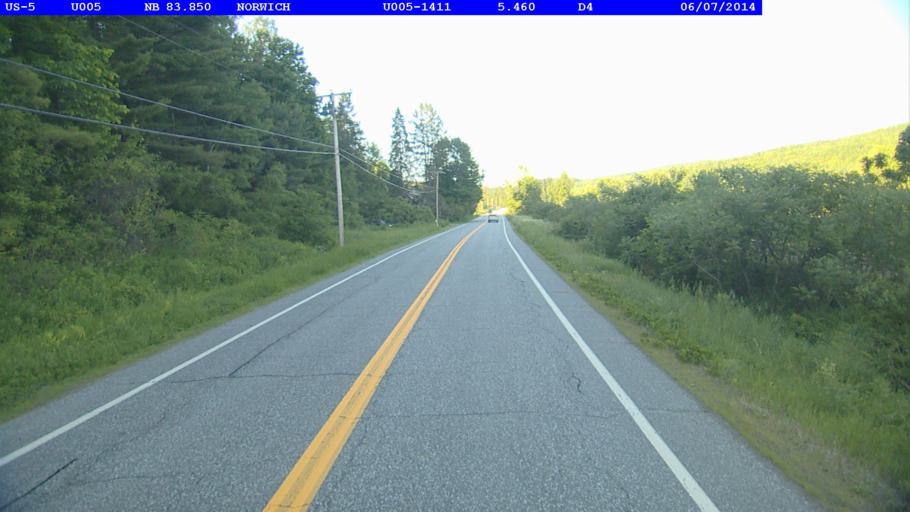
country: US
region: New Hampshire
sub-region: Grafton County
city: Hanover
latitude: 43.7441
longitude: -72.2450
